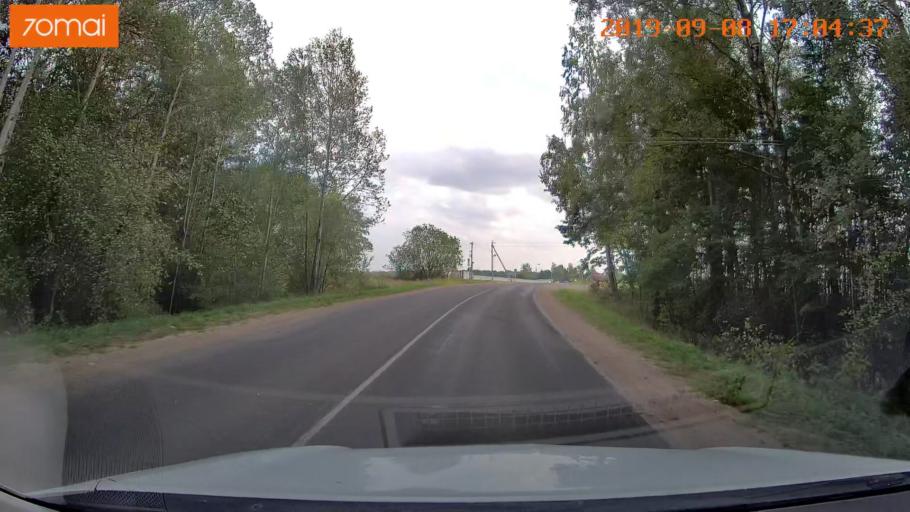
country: BY
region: Grodnenskaya
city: Hrodna
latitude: 53.6881
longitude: 23.9549
